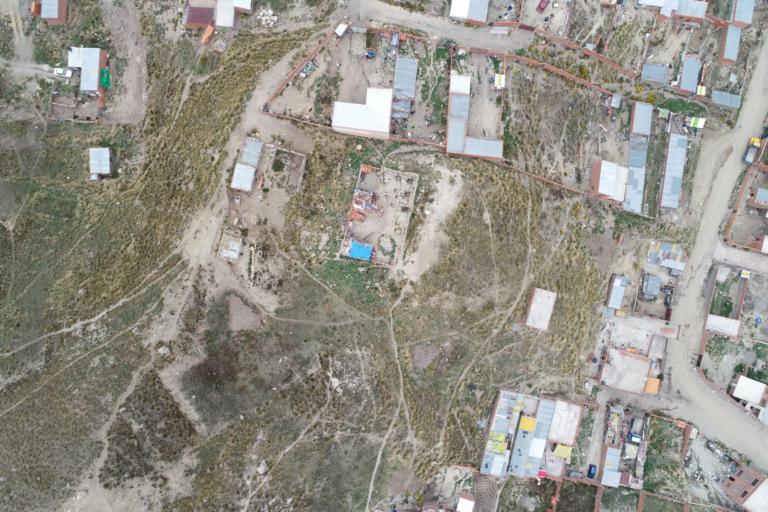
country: BO
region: La Paz
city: La Paz
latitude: -16.4418
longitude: -68.1428
